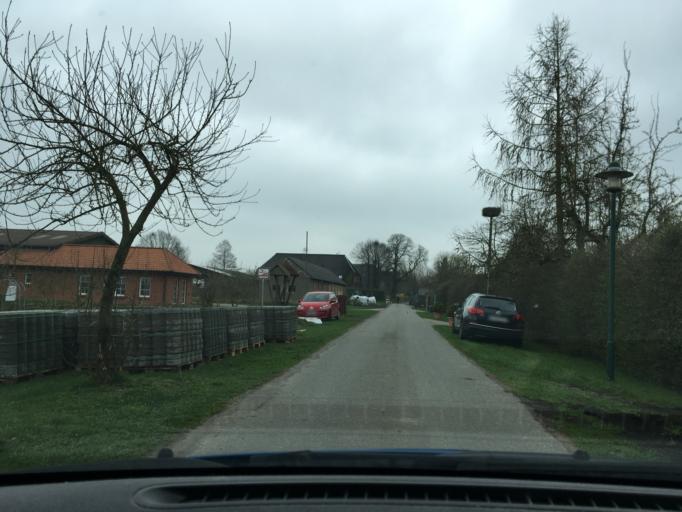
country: DE
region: Lower Saxony
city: Bleckede
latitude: 53.2916
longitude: 10.7977
